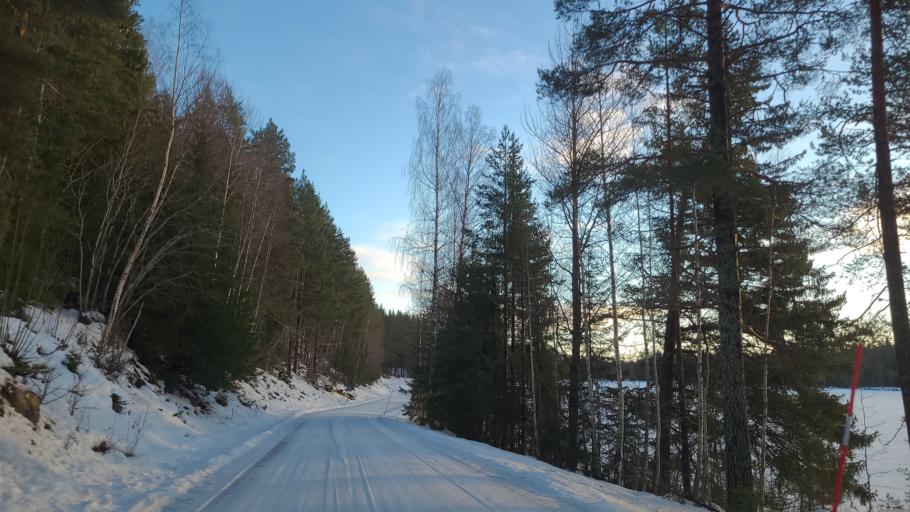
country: SE
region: Gaevleborg
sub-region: Bollnas Kommun
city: Kilafors
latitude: 61.3893
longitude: 16.6853
